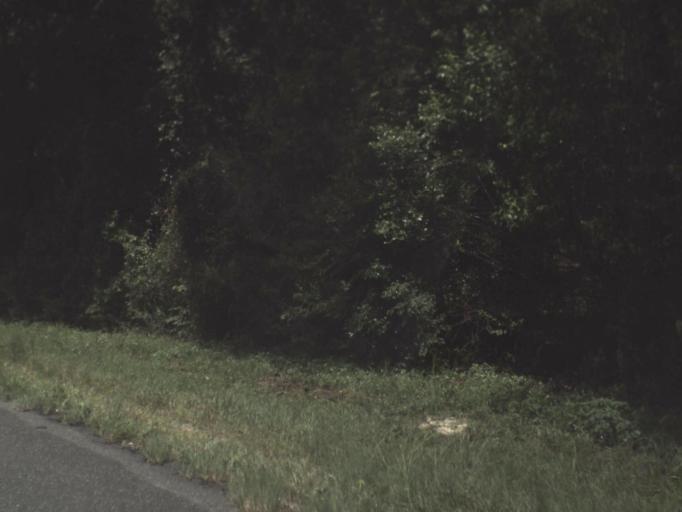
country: US
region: Florida
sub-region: Alachua County
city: Archer
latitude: 29.5883
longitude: -82.5591
